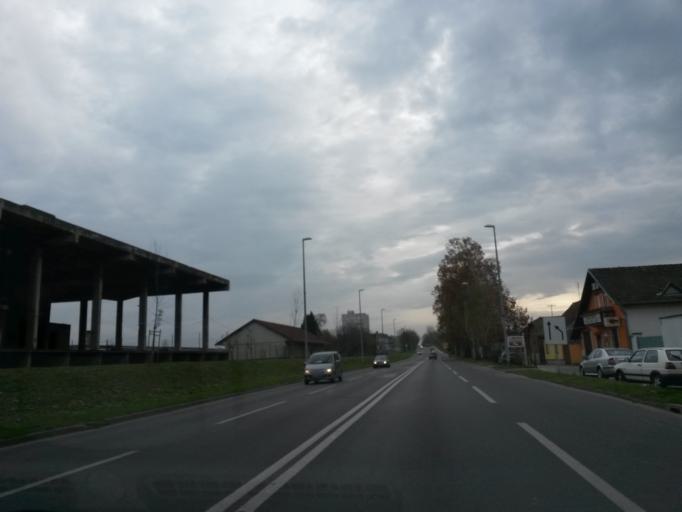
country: HR
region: Vukovarsko-Srijemska
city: Borovo
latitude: 45.3627
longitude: 18.9852
